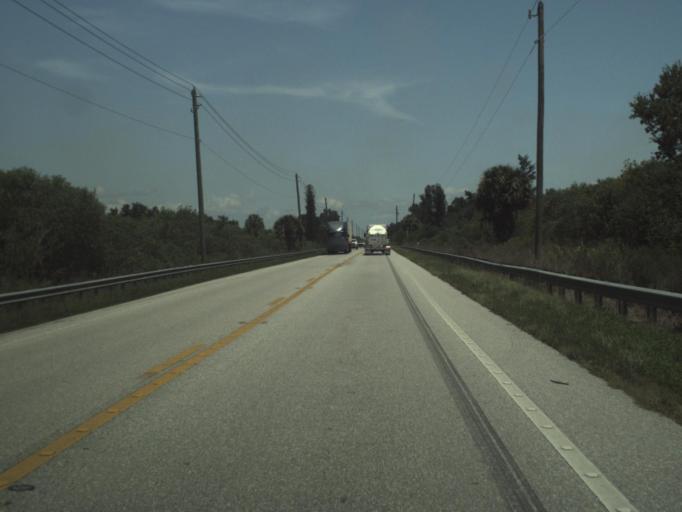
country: US
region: Florida
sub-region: Martin County
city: Indiantown
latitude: 27.0865
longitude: -80.5679
